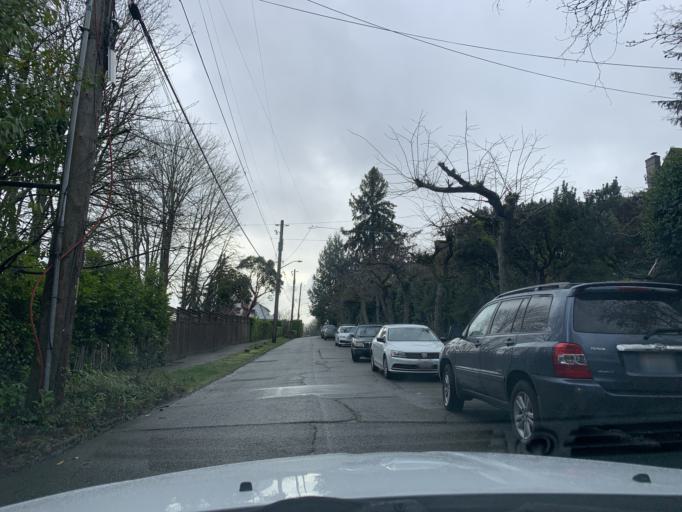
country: US
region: Washington
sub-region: King County
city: Seattle
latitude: 47.6089
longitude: -122.2861
